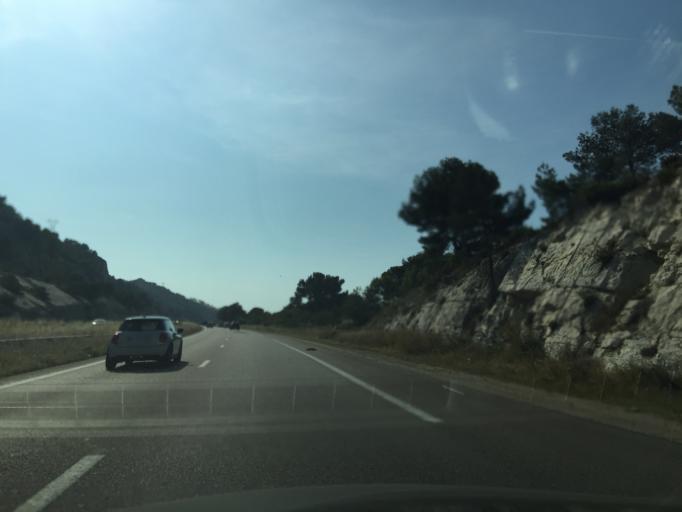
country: FR
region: Provence-Alpes-Cote d'Azur
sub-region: Departement des Bouches-du-Rhone
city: Chateauneuf-les-Martigues
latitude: 43.3783
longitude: 5.1699
